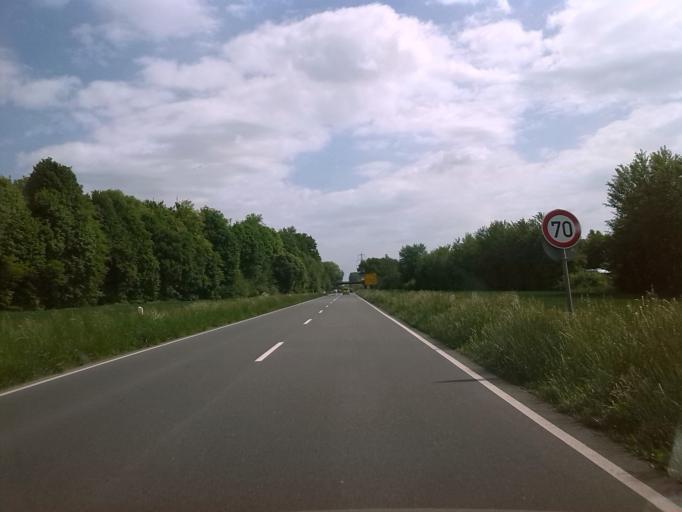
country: DE
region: Hesse
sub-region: Regierungsbezirk Darmstadt
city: Gross-Zimmern
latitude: 49.8813
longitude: 8.8084
